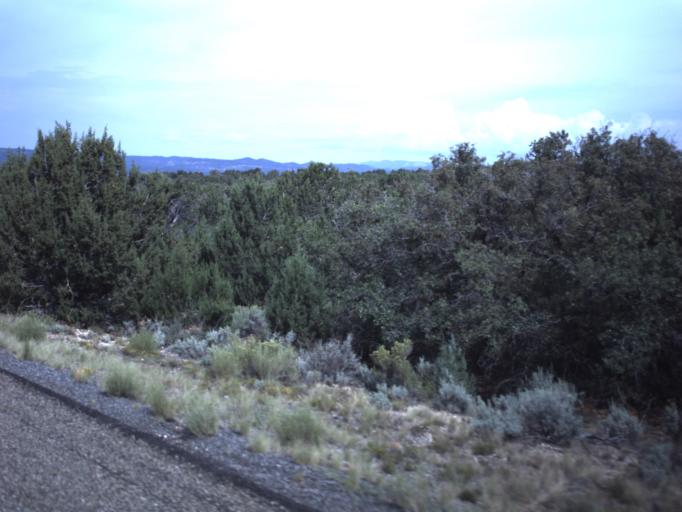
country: US
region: Utah
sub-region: Kane County
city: Kanab
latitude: 37.1818
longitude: -112.6402
